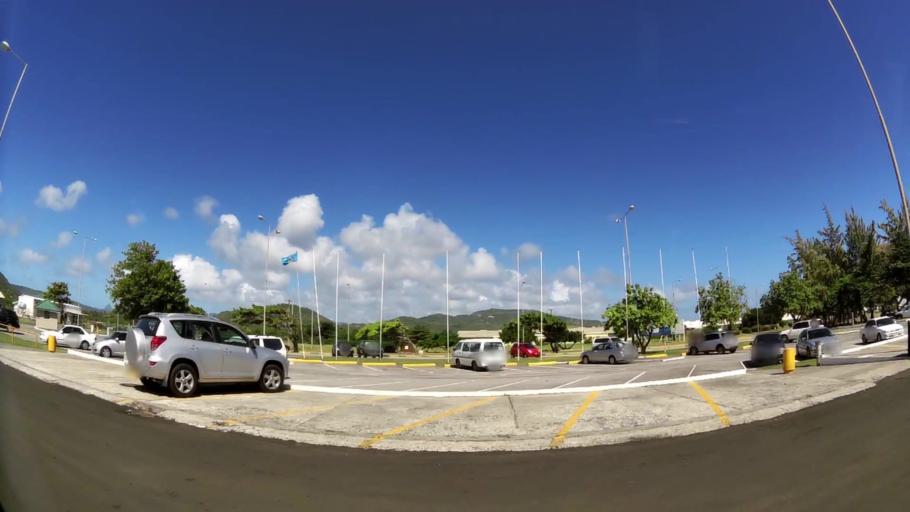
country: LC
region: Vieux-Fort
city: Vieux Fort
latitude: 13.7368
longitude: -60.9505
